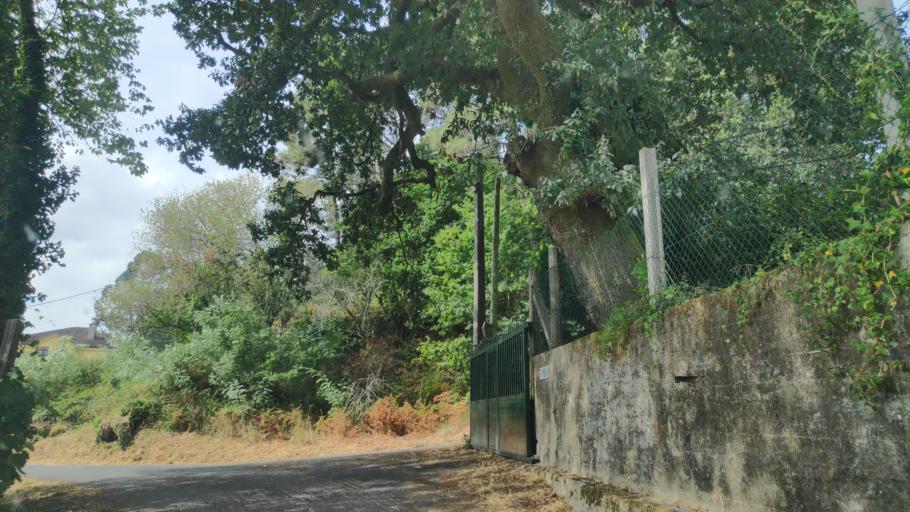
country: ES
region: Galicia
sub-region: Provincia da Coruna
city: Padron
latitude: 42.7283
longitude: -8.6746
